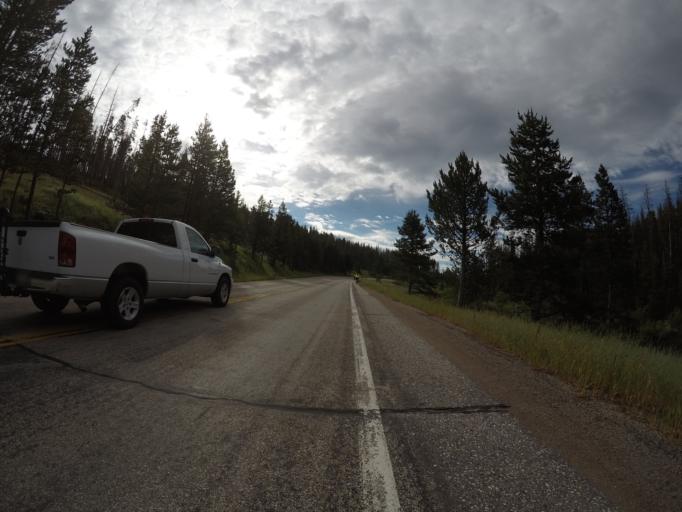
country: US
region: Wyoming
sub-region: Carbon County
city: Saratoga
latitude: 41.3273
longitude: -106.5090
